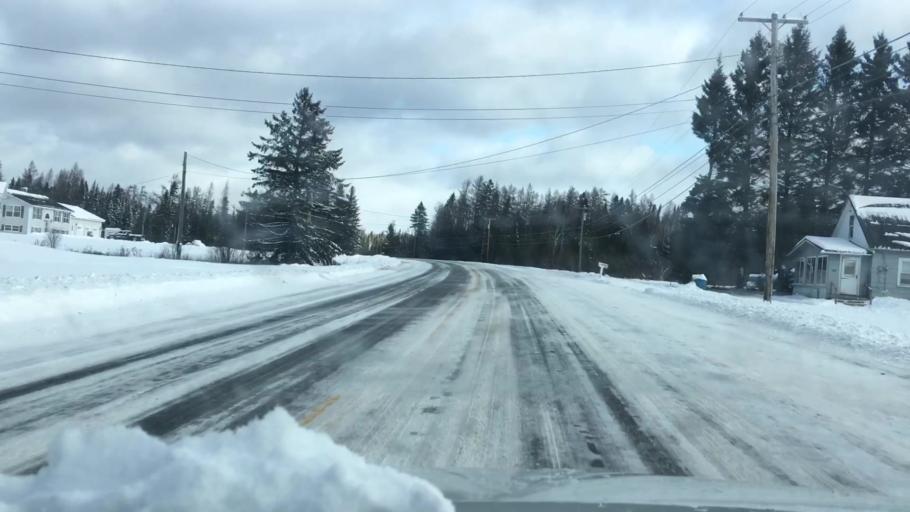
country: US
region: Maine
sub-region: Aroostook County
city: Madawaska
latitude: 46.9990
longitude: -68.0250
